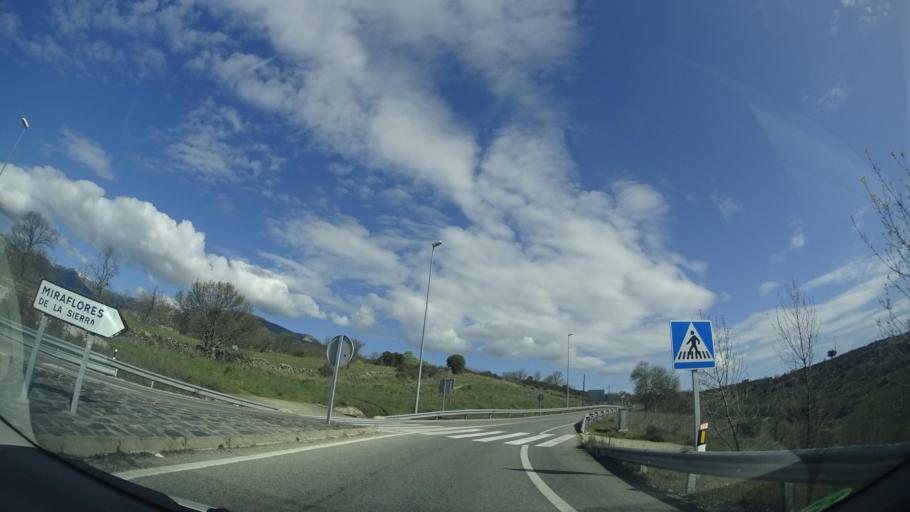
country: ES
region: Madrid
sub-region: Provincia de Madrid
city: Miraflores de la Sierra
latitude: 40.7701
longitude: -3.7799
